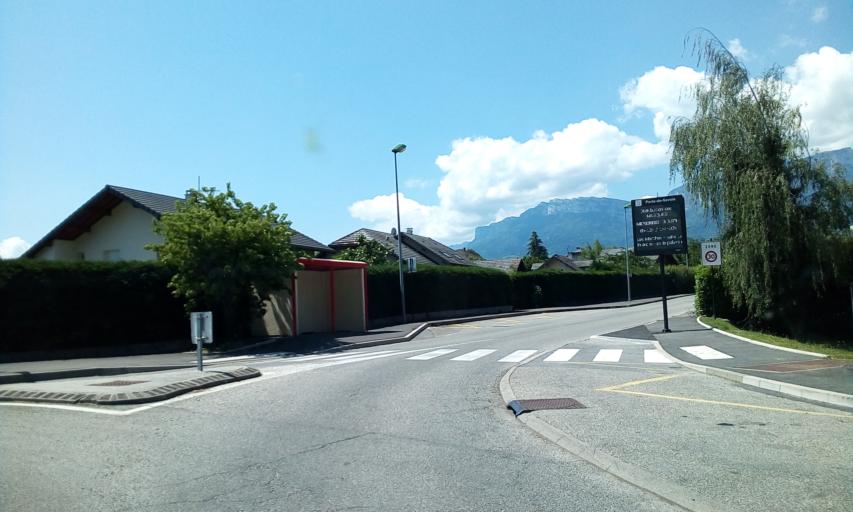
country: FR
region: Rhone-Alpes
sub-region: Departement de la Savoie
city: Montmelian
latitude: 45.5012
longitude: 6.0276
